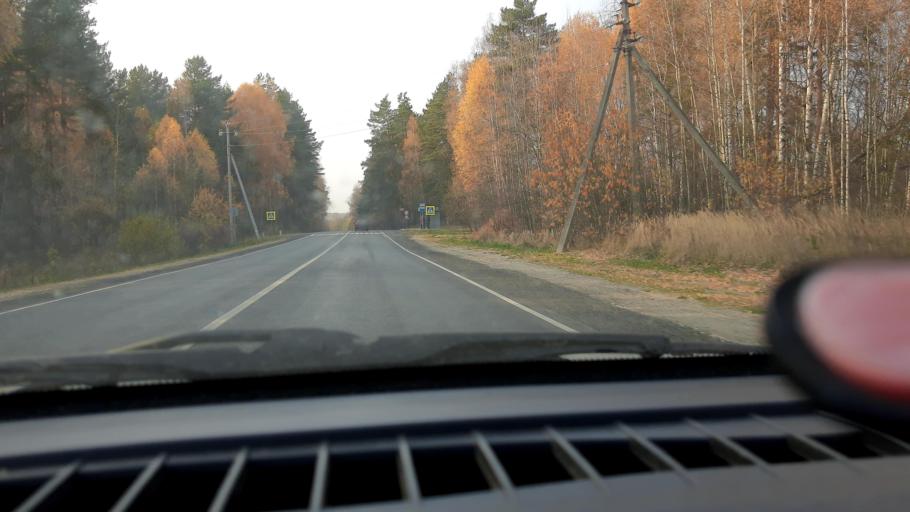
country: RU
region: Nizjnij Novgorod
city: Novaya Balakhna
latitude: 56.6134
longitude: 43.5906
